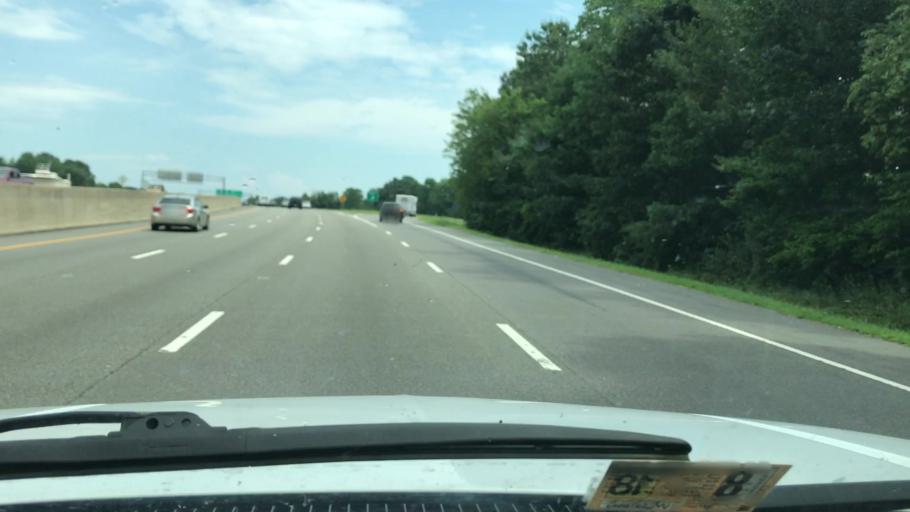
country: US
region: Virginia
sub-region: Chesterfield County
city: Bensley
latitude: 37.4519
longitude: -77.4901
